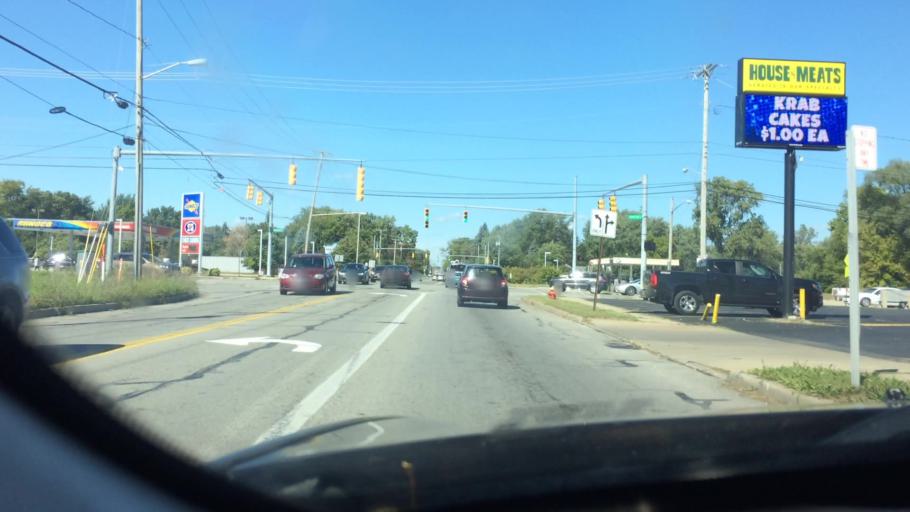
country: US
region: Ohio
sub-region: Lucas County
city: Ottawa Hills
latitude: 41.6611
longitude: -83.6825
